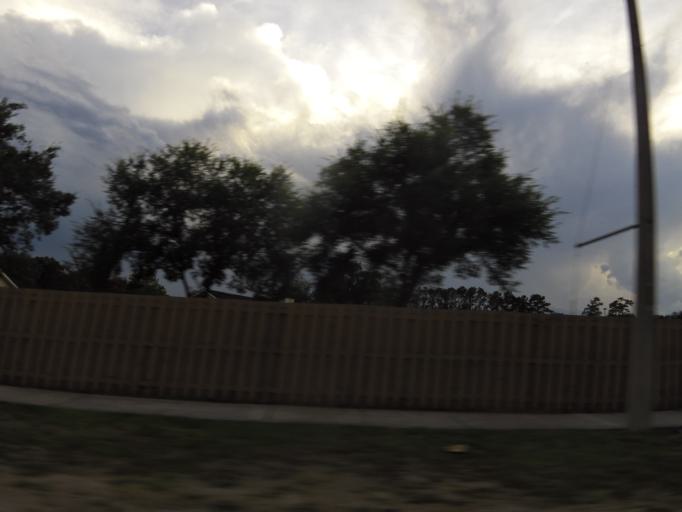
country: US
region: Florida
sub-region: Clay County
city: Bellair-Meadowbrook Terrace
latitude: 30.2987
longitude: -81.7983
